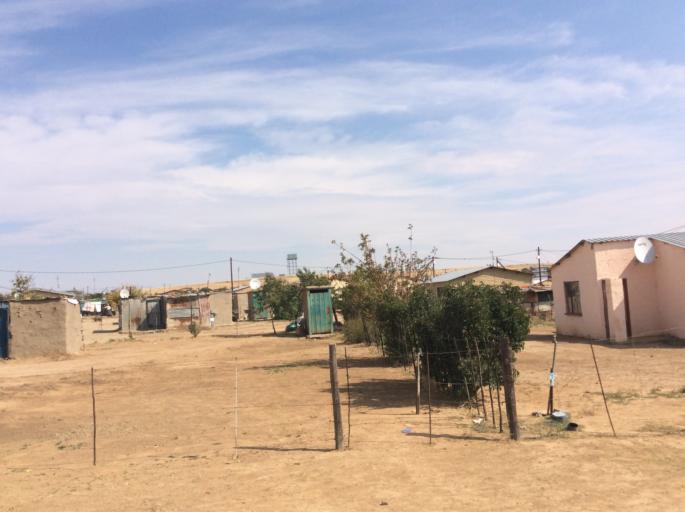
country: ZA
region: Orange Free State
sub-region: Xhariep District Municipality
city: Dewetsdorp
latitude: -29.5940
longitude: 26.6809
